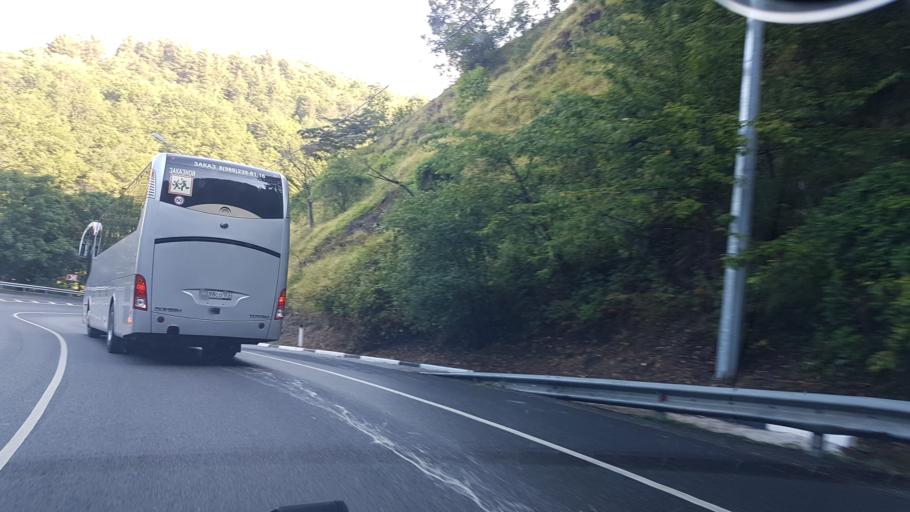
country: RU
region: Krasnodarskiy
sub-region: Sochi City
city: Lazarevskoye
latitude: 43.8419
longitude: 39.4173
